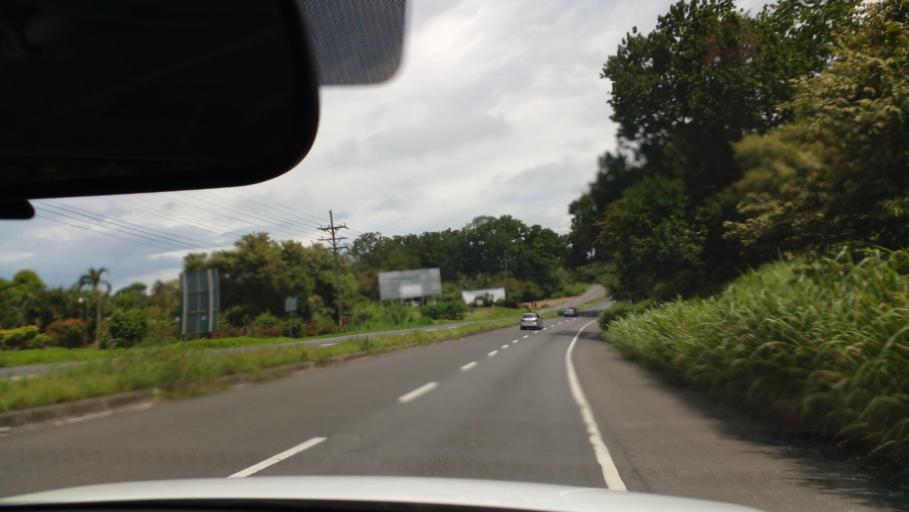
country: PA
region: Panama
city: Nueva Gorgona
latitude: 8.4781
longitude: -79.9584
